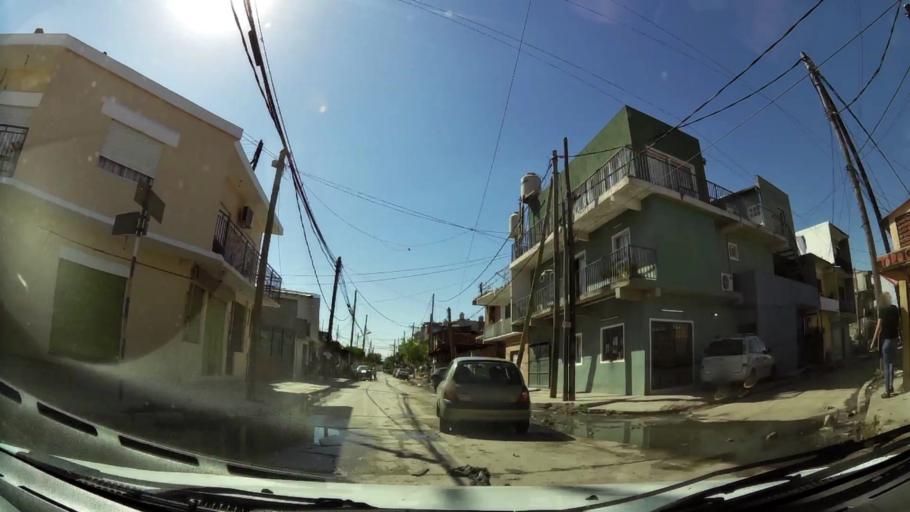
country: AR
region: Buenos Aires
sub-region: Partido de General San Martin
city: General San Martin
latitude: -34.5330
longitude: -58.5818
